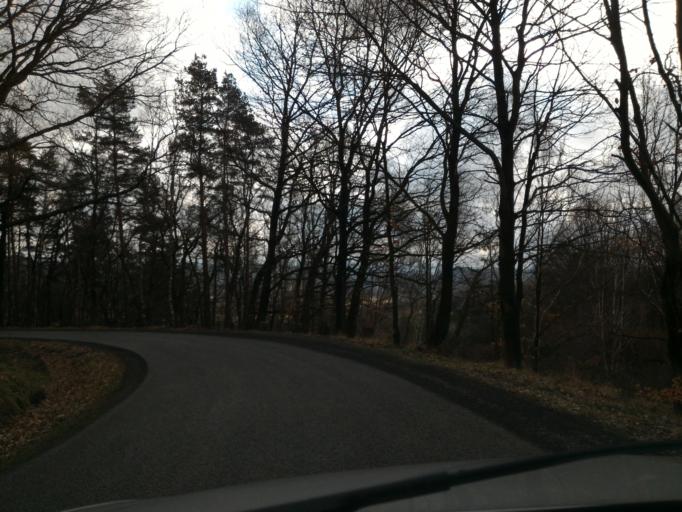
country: CZ
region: Liberecky
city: Visnova
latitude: 50.9926
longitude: 15.0199
